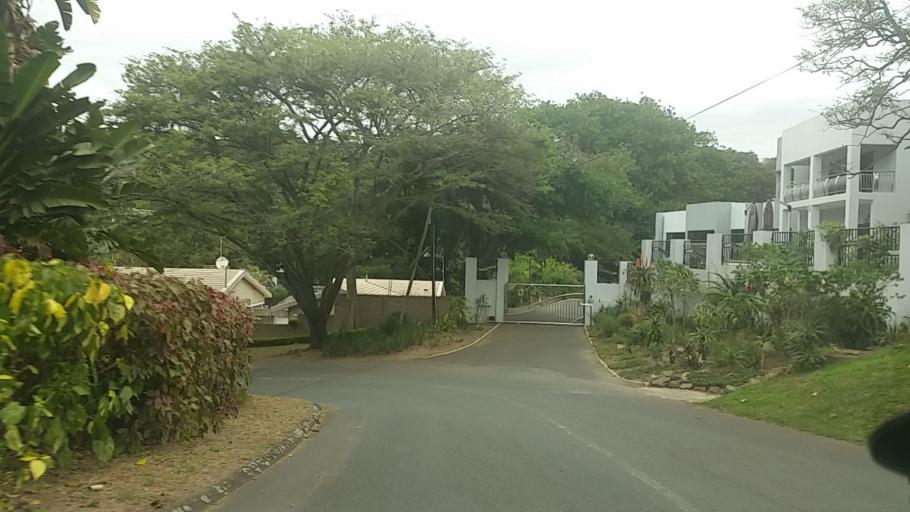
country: ZA
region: KwaZulu-Natal
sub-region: eThekwini Metropolitan Municipality
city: Berea
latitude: -29.8383
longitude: 30.9295
